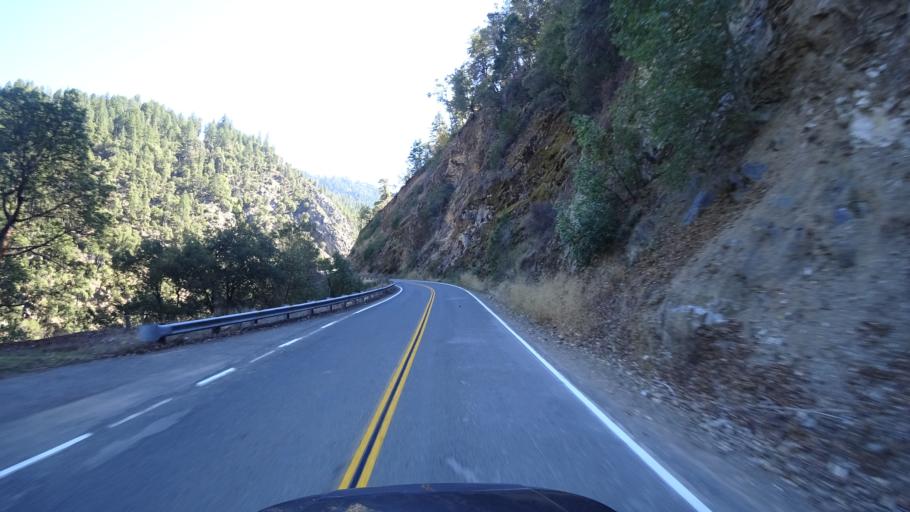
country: US
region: California
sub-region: Siskiyou County
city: Happy Camp
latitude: 41.3741
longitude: -123.4194
